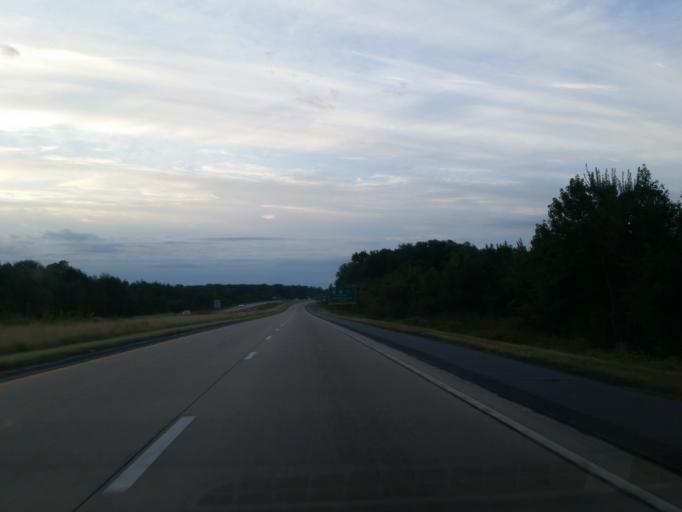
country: US
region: Delaware
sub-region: Kent County
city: Cheswold
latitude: 39.2145
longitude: -75.5538
